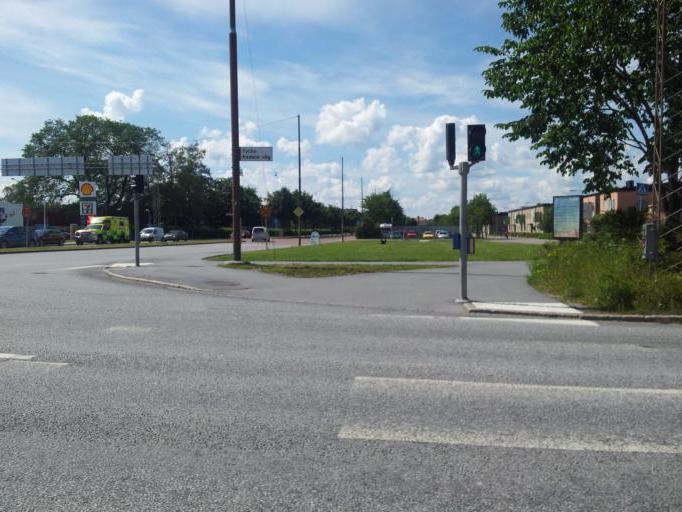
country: SE
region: Uppsala
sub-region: Uppsala Kommun
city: Uppsala
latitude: 59.8683
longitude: 17.6595
